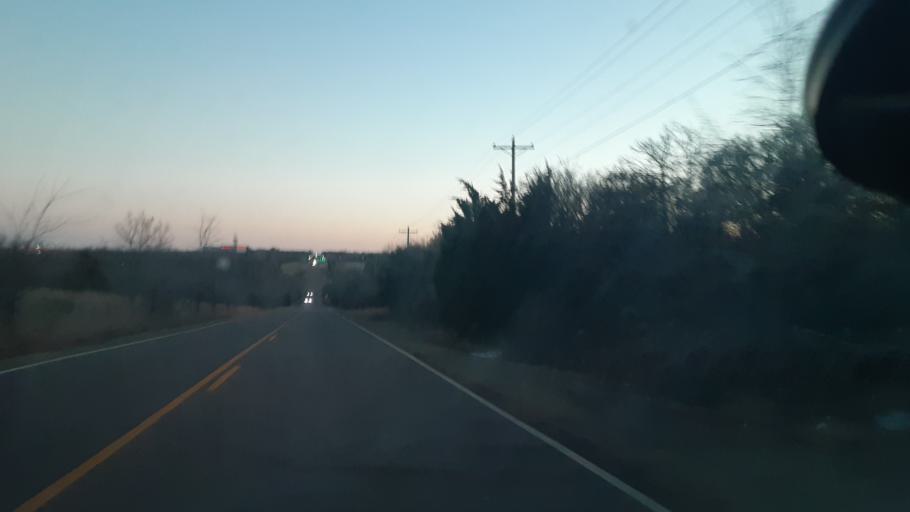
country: US
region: Oklahoma
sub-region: Oklahoma County
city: Edmond
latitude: 35.6926
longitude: -97.4251
